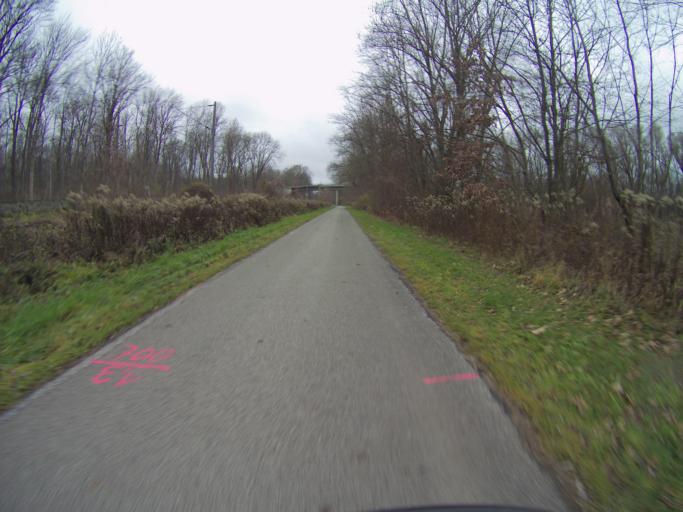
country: DE
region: Bavaria
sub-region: Upper Bavaria
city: Marzling
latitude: 48.4081
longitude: 11.7808
